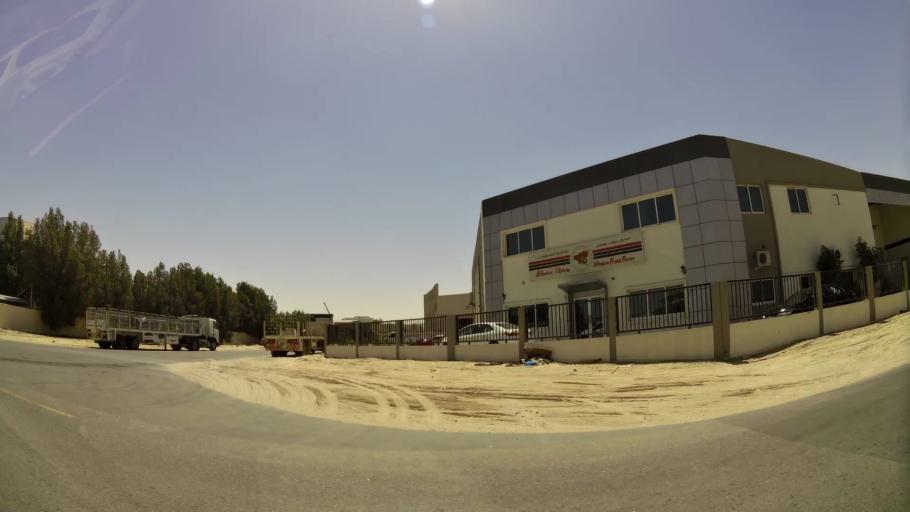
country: AE
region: Dubai
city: Dubai
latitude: 24.9885
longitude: 55.1940
